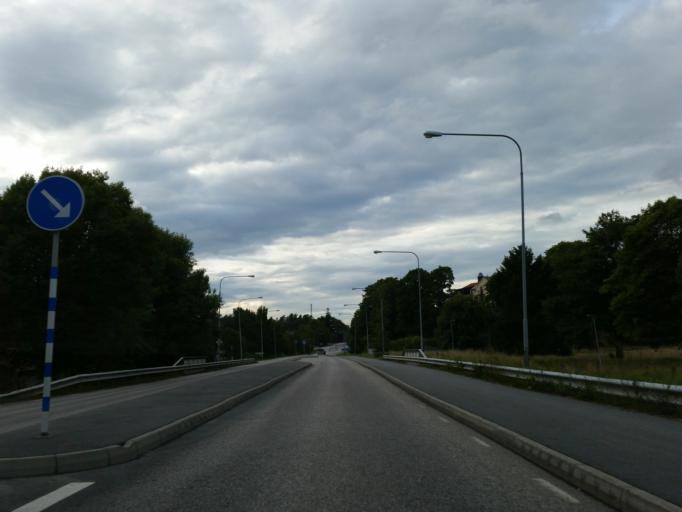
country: SE
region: Stockholm
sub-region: Upplands Vasby Kommun
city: Upplands Vaesby
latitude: 59.5385
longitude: 17.9158
